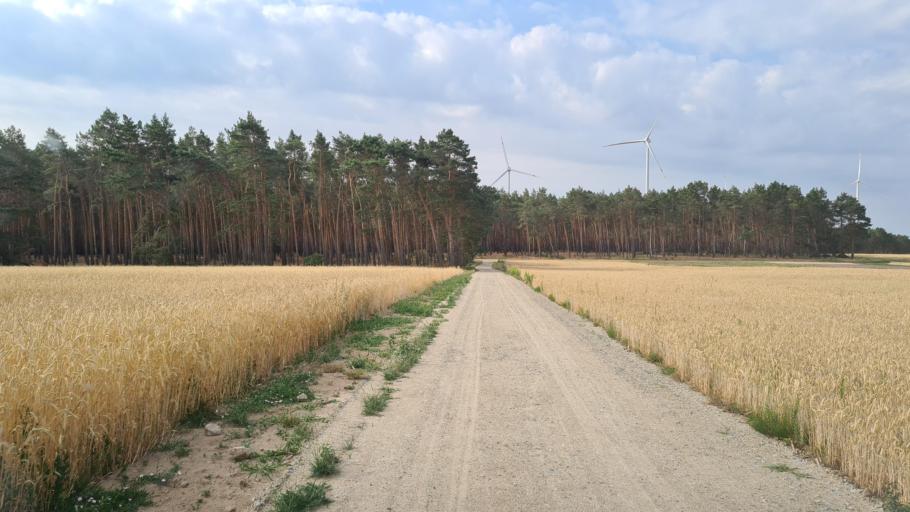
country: DE
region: Brandenburg
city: Linthe
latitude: 52.1035
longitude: 12.8087
